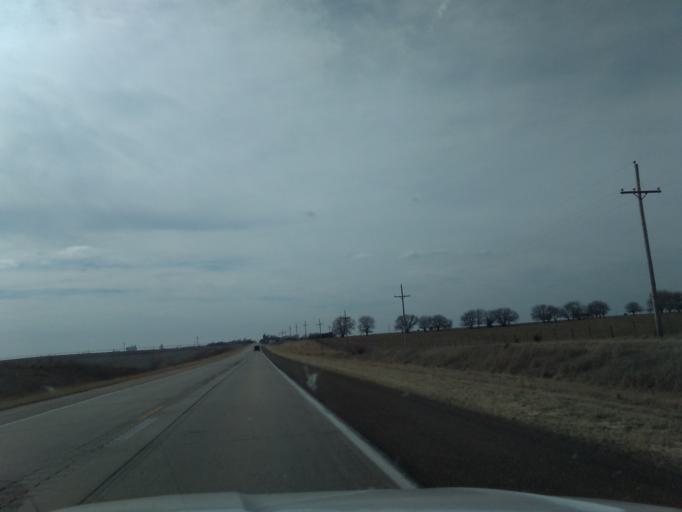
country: US
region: Nebraska
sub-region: Jefferson County
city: Fairbury
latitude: 40.1900
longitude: -97.0238
